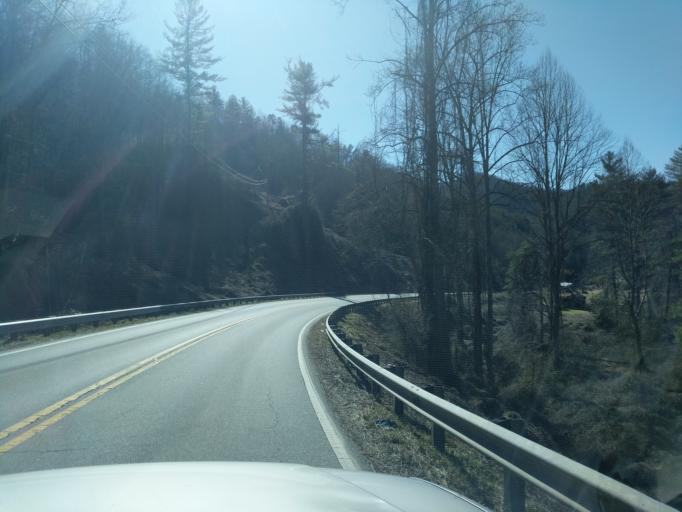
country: US
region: North Carolina
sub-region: Swain County
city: Bryson City
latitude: 35.3318
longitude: -83.5758
